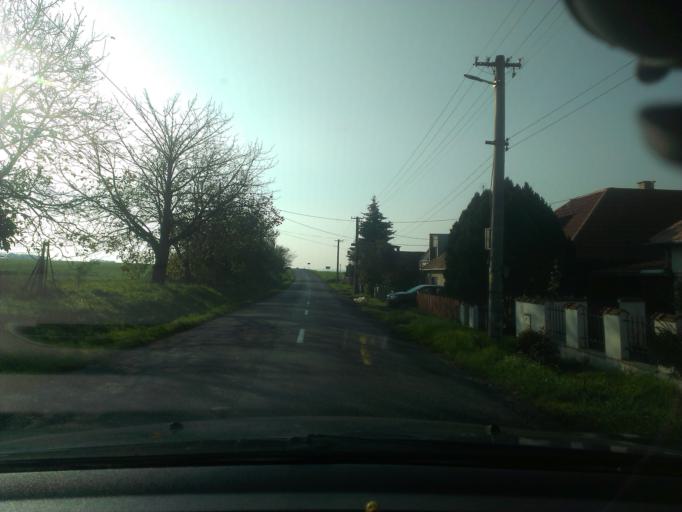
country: SK
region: Nitriansky
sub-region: Okres Nitra
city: Nitra
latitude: 48.4575
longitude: 17.9848
